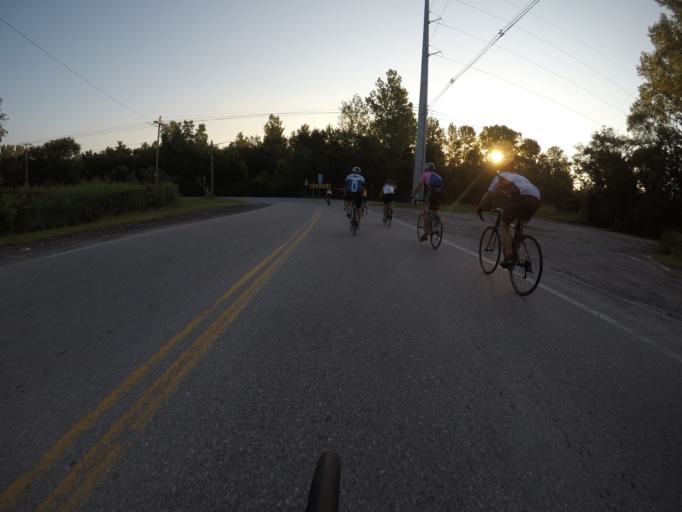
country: US
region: Missouri
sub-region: Platte County
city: Weatherby Lake
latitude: 39.1876
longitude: -94.8010
